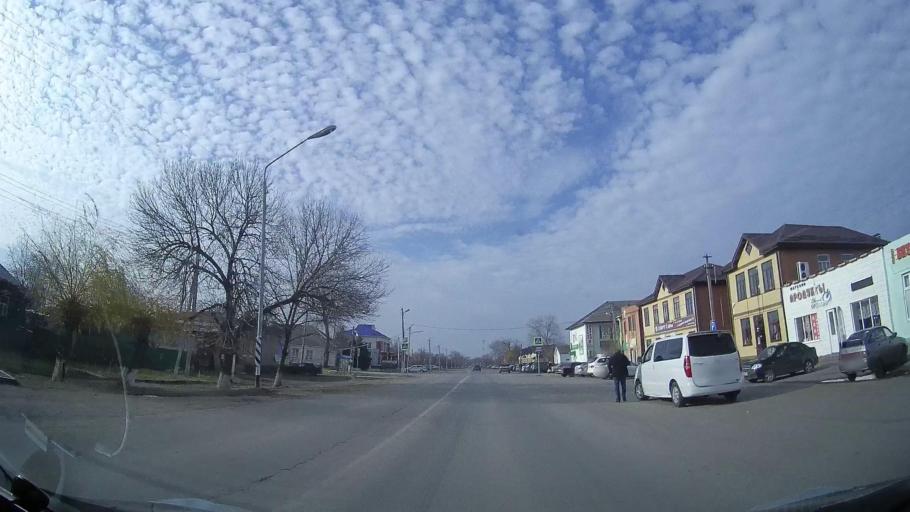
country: RU
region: Rostov
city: Veselyy
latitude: 47.0914
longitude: 40.7428
